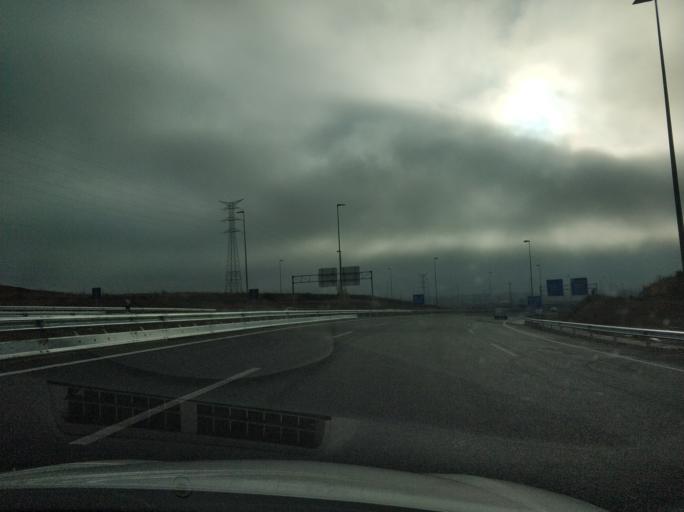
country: ES
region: Castille and Leon
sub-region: Provincia de Leon
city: Leon
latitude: 42.5733
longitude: -5.5404
